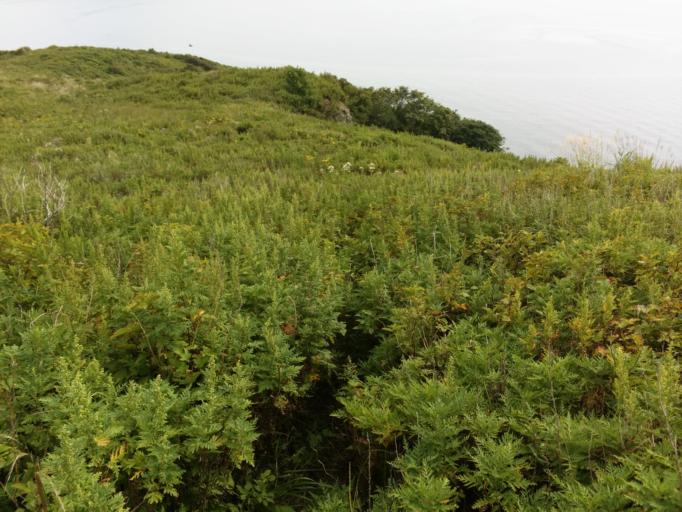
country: RU
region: Primorskiy
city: Popova
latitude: 42.9209
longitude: 131.7111
